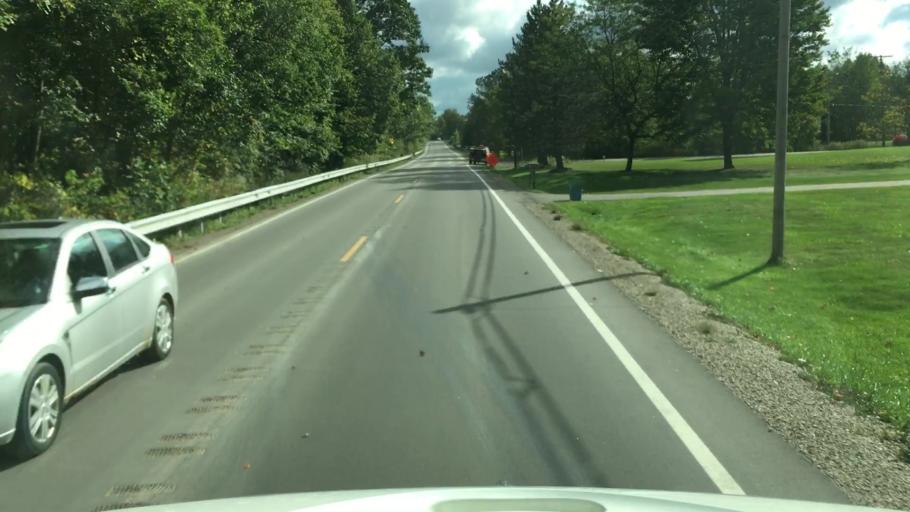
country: US
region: Michigan
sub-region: Oakland County
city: Ortonville
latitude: 42.8669
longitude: -83.3819
